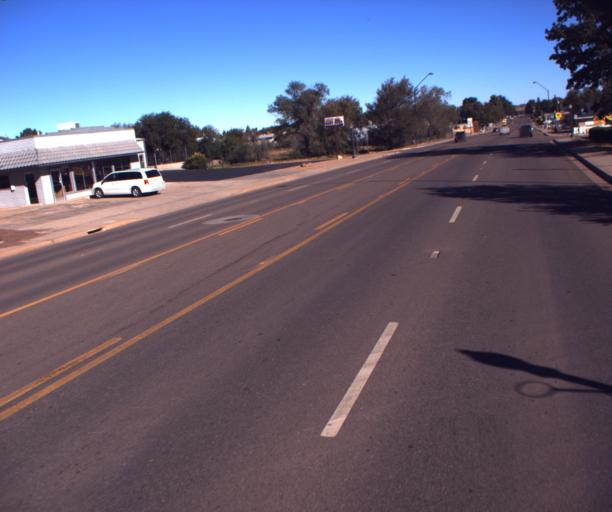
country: US
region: Arizona
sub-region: Navajo County
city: Snowflake
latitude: 34.5043
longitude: -110.0790
